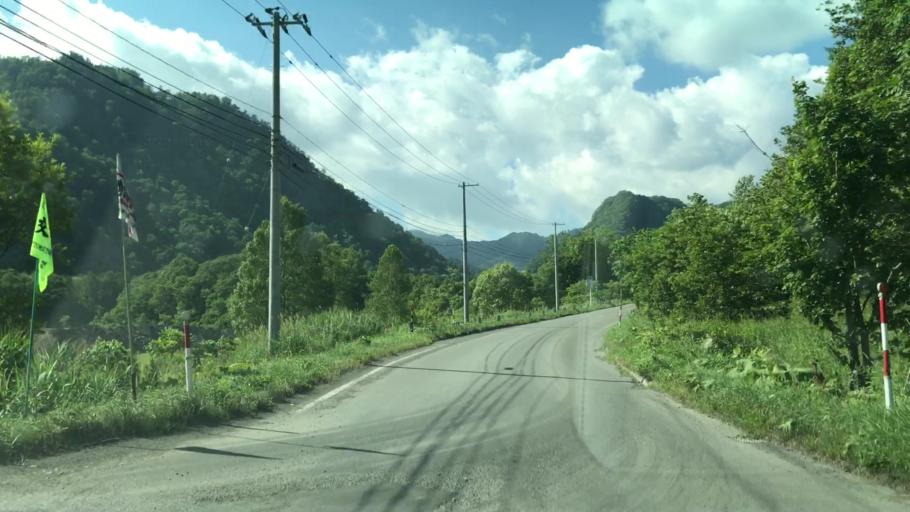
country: JP
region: Hokkaido
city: Shimo-furano
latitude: 42.8481
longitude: 142.4222
